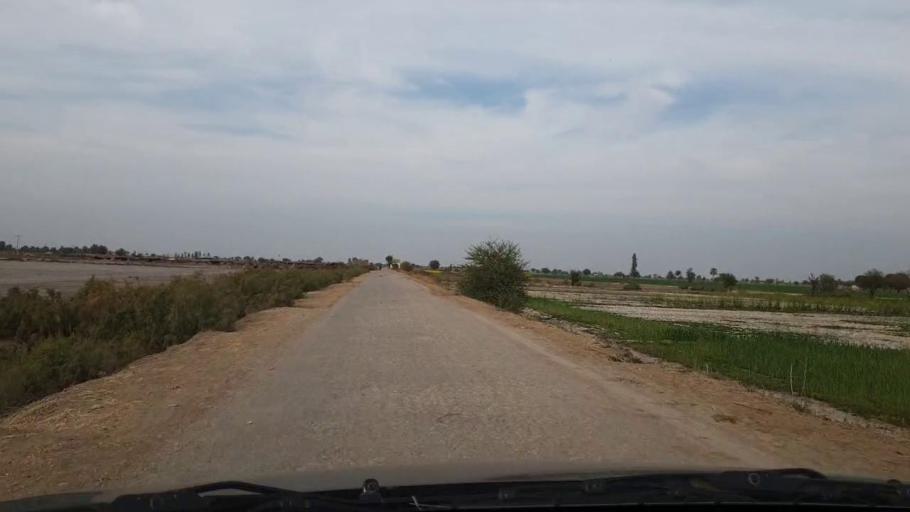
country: PK
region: Sindh
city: Khadro
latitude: 26.1577
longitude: 68.7304
